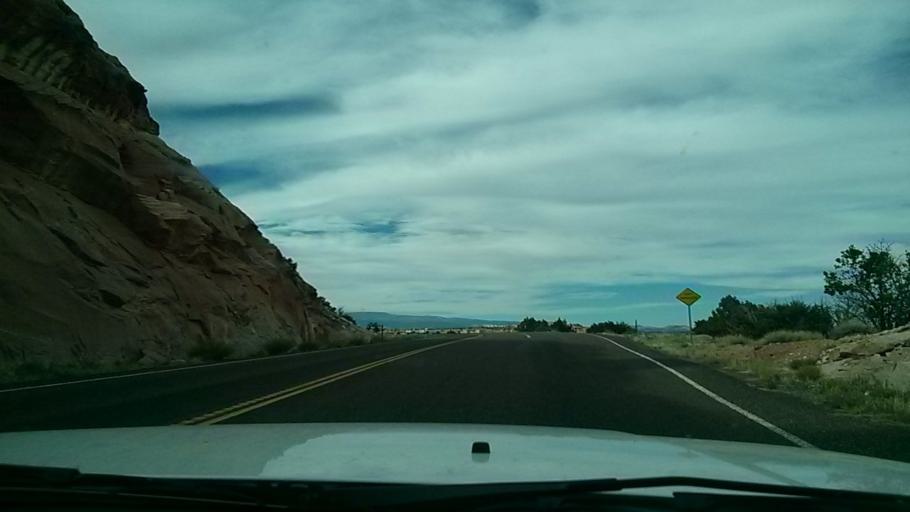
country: US
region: Utah
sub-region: Wayne County
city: Loa
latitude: 37.7449
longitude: -111.4547
